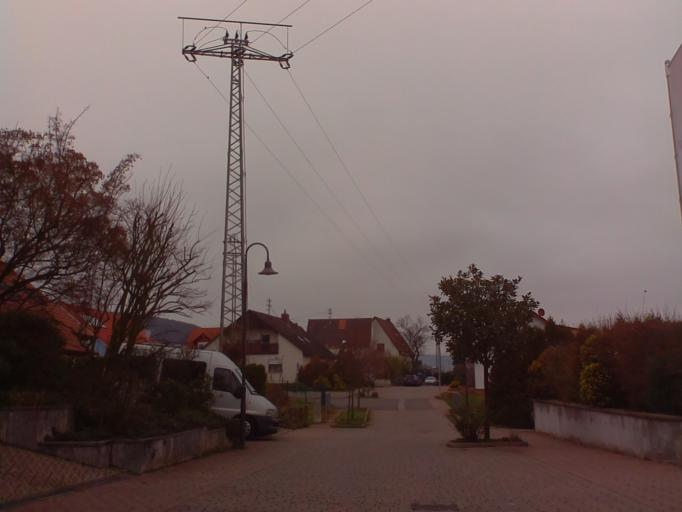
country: DE
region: Rheinland-Pfalz
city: Maikammer
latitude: 49.3217
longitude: 8.1318
